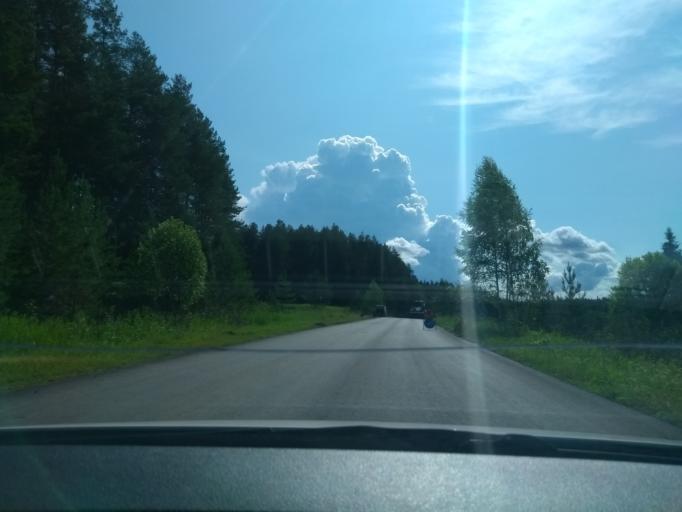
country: RU
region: Perm
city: Bershet'
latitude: 57.8209
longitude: 56.5216
